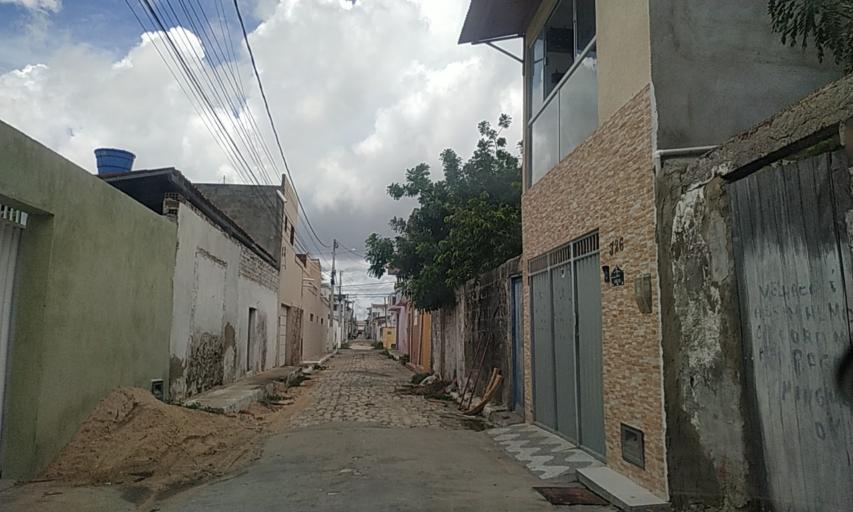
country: BR
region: Rio Grande do Norte
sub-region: Areia Branca
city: Areia Branca
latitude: -4.9530
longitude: -37.1346
